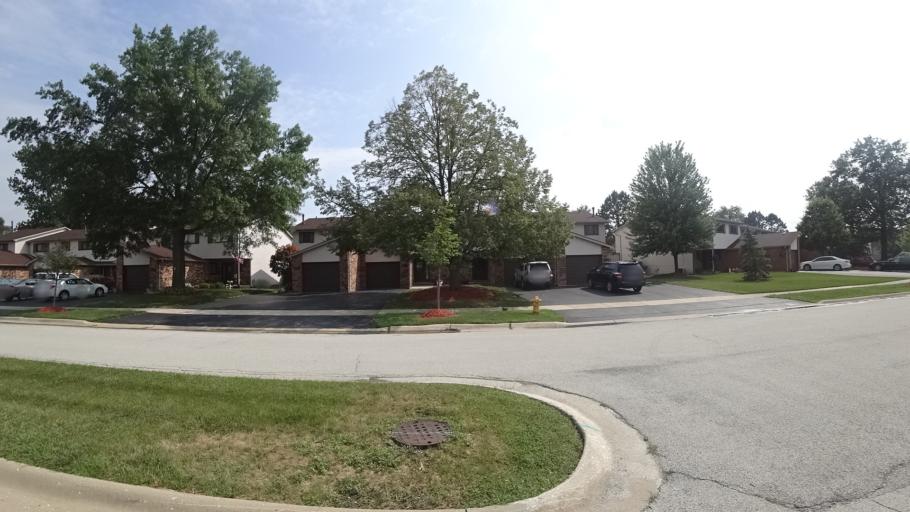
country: US
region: Illinois
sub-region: Cook County
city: Tinley Park
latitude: 41.5952
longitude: -87.7869
